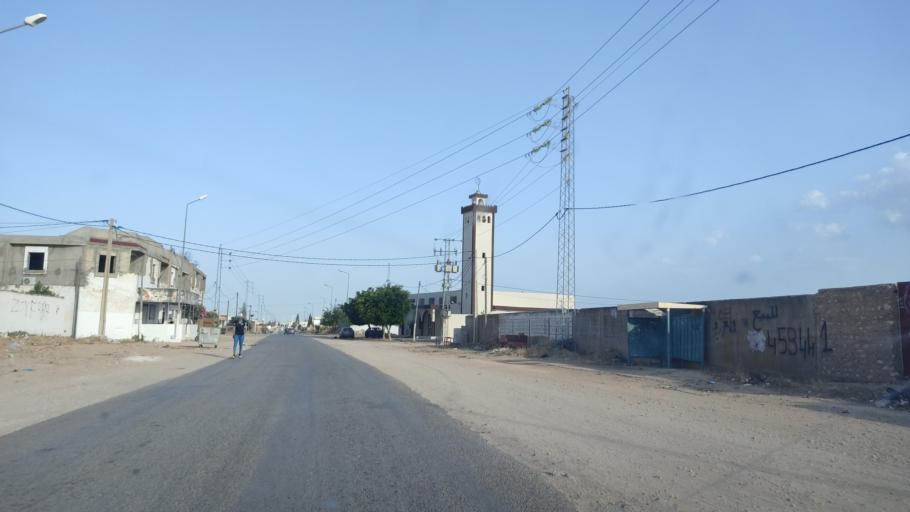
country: TN
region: Safaqis
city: Sfax
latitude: 34.8018
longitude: 10.6721
